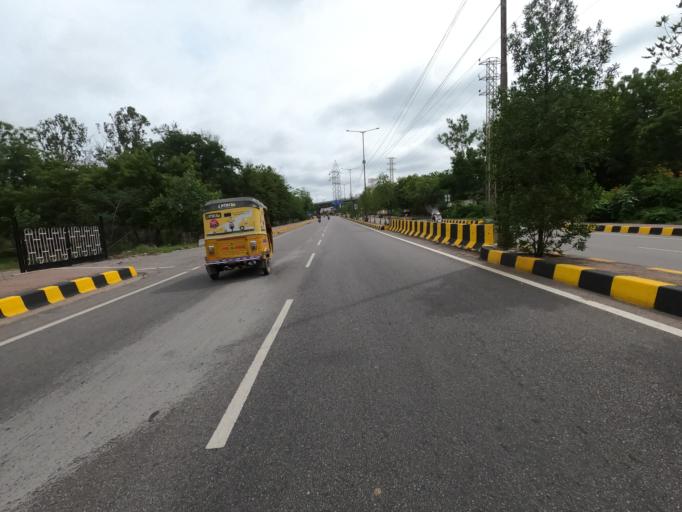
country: IN
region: Telangana
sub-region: Hyderabad
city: Hyderabad
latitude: 17.3438
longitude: 78.4149
